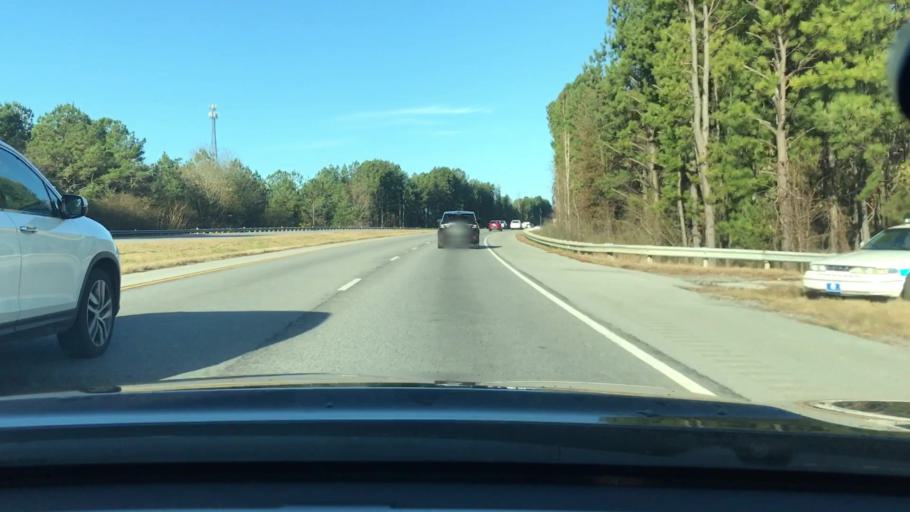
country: US
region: Alabama
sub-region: Shelby County
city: Chelsea
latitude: 33.3486
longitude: -86.6400
